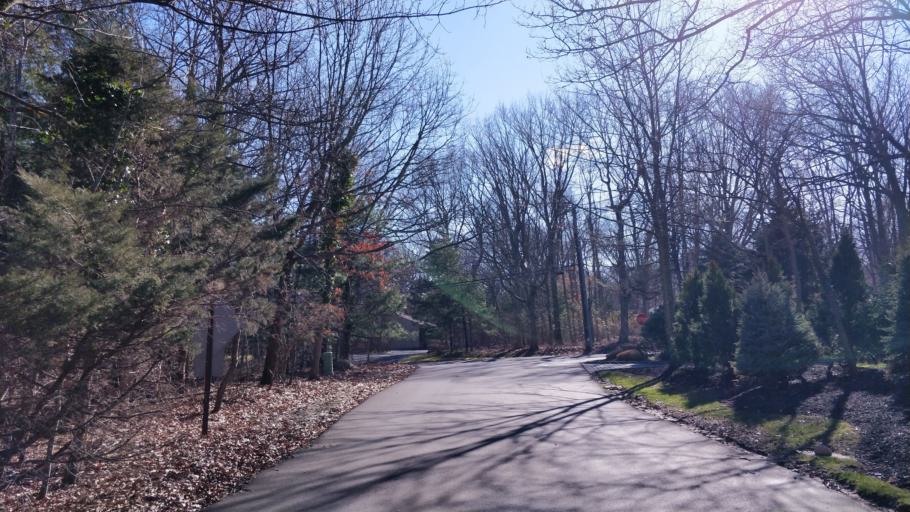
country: US
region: New York
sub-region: Suffolk County
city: Port Jefferson
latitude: 40.9658
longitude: -73.0665
